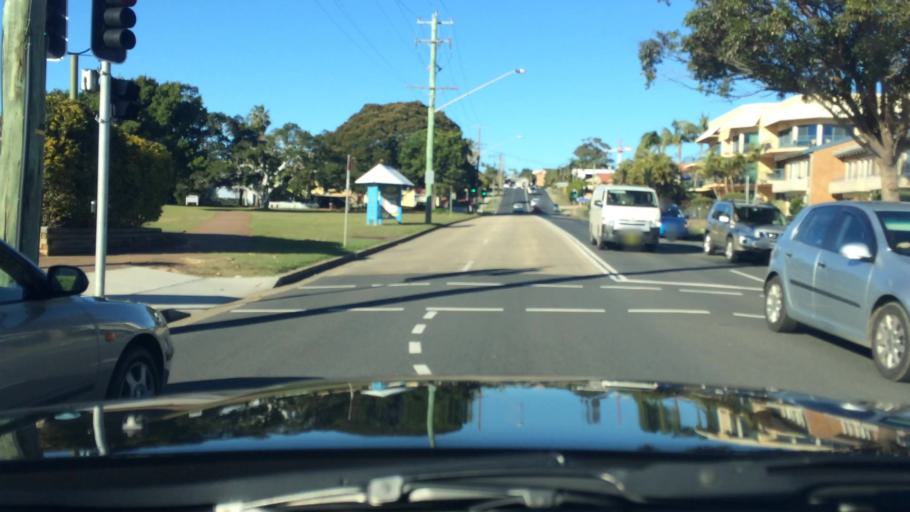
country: AU
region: New South Wales
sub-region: Port Macquarie-Hastings
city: Port Macquarie
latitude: -31.4302
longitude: 152.8999
